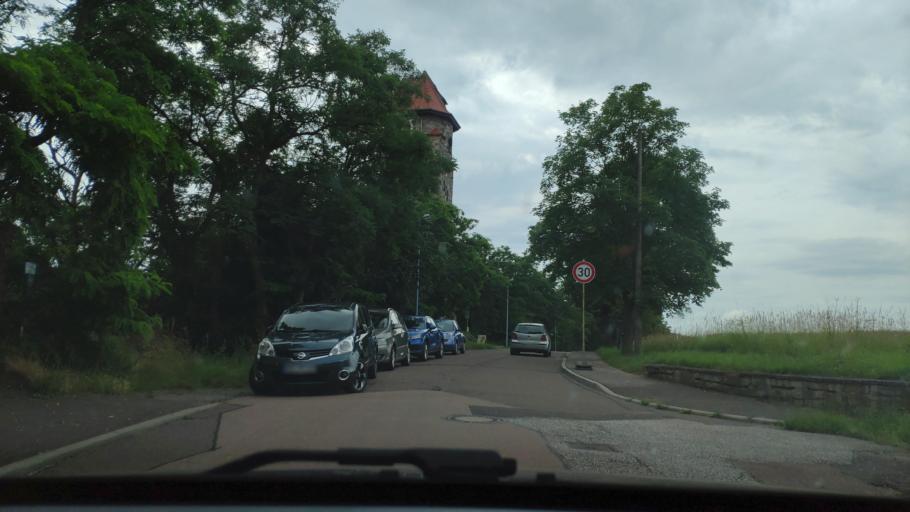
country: DE
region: Saxony-Anhalt
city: Bernburg
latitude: 51.7935
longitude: 11.7164
